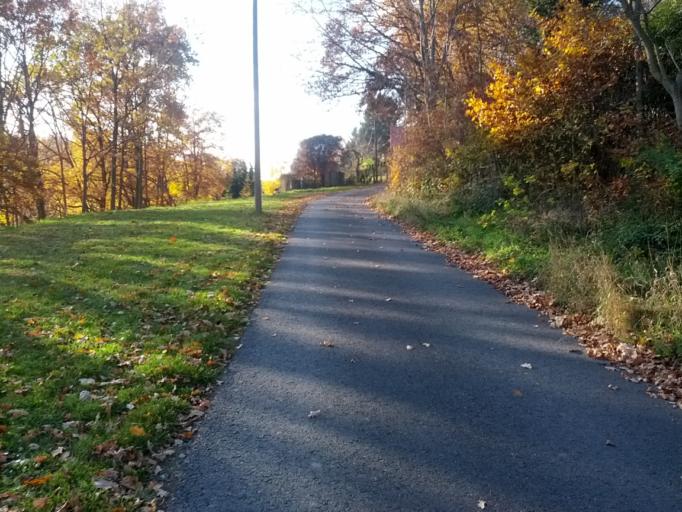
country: DE
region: Thuringia
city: Thal
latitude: 50.9360
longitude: 10.3873
